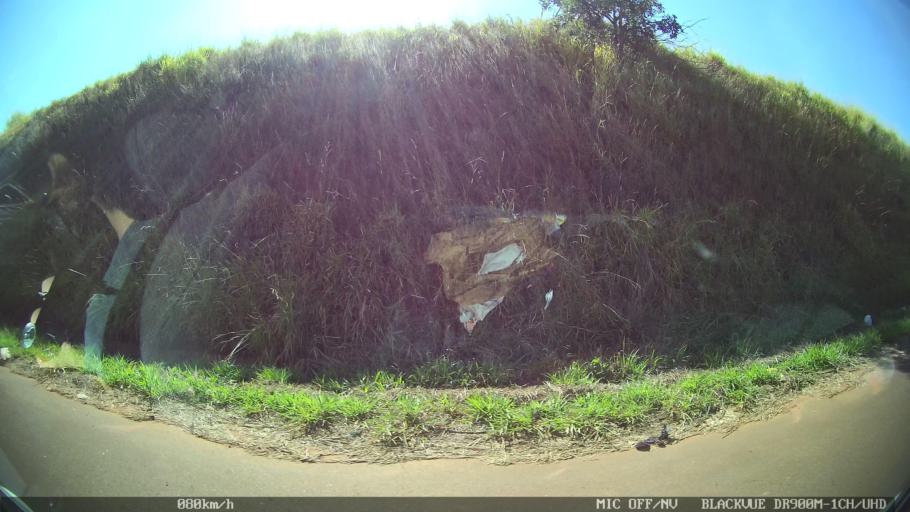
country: BR
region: Sao Paulo
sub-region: Batatais
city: Batatais
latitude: -20.8759
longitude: -47.6071
